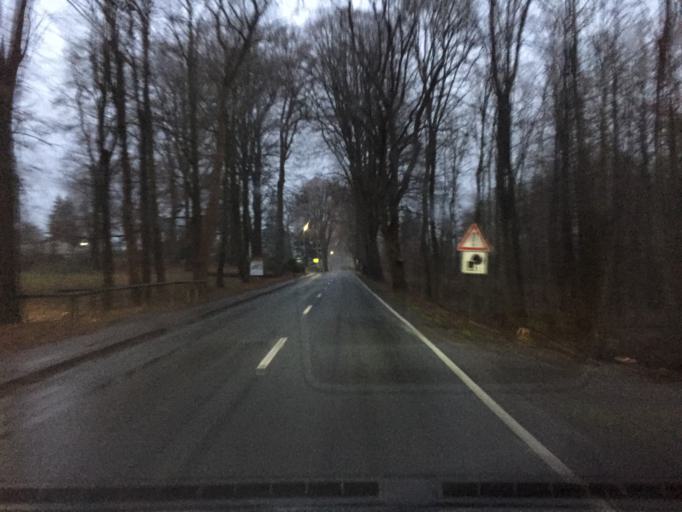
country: DE
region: Lower Saxony
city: Sudwalde
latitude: 52.8371
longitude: 8.8427
